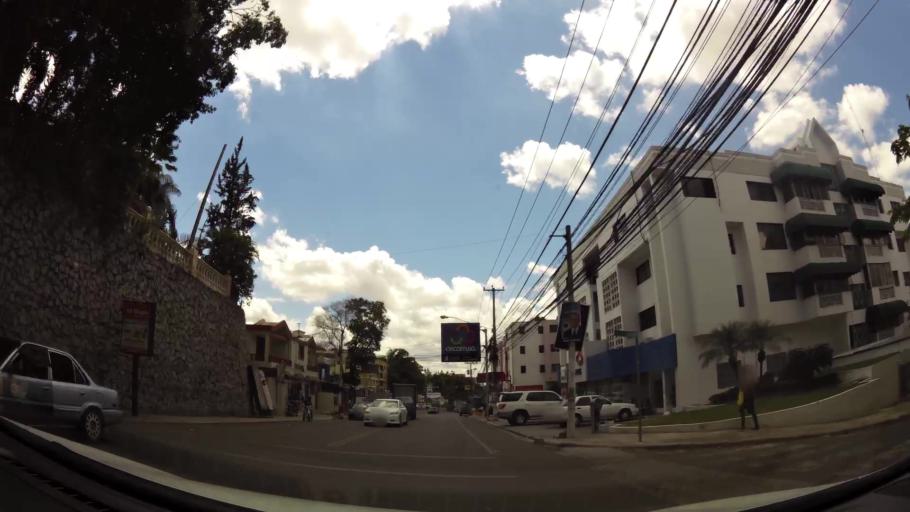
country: DO
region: Santiago
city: Santiago de los Caballeros
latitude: 19.4719
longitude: -70.6817
